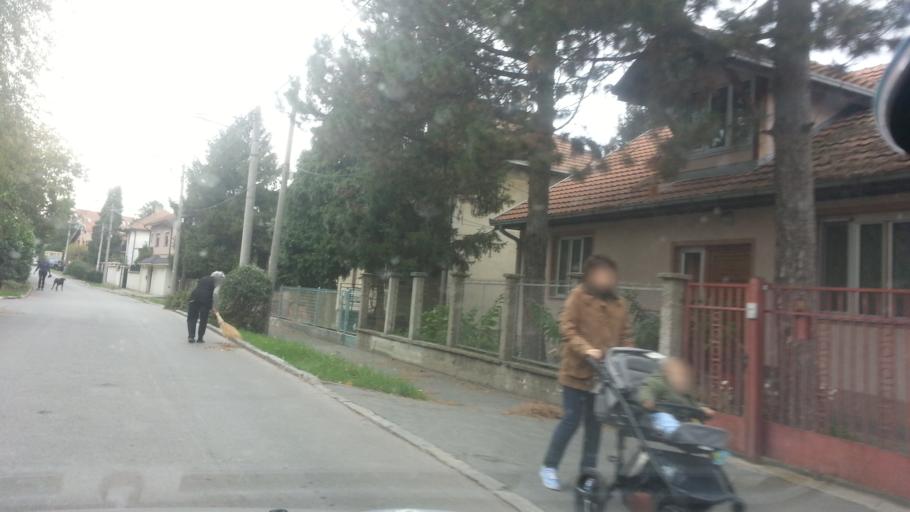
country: RS
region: Central Serbia
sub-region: Belgrade
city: Zemun
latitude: 44.8372
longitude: 20.3990
